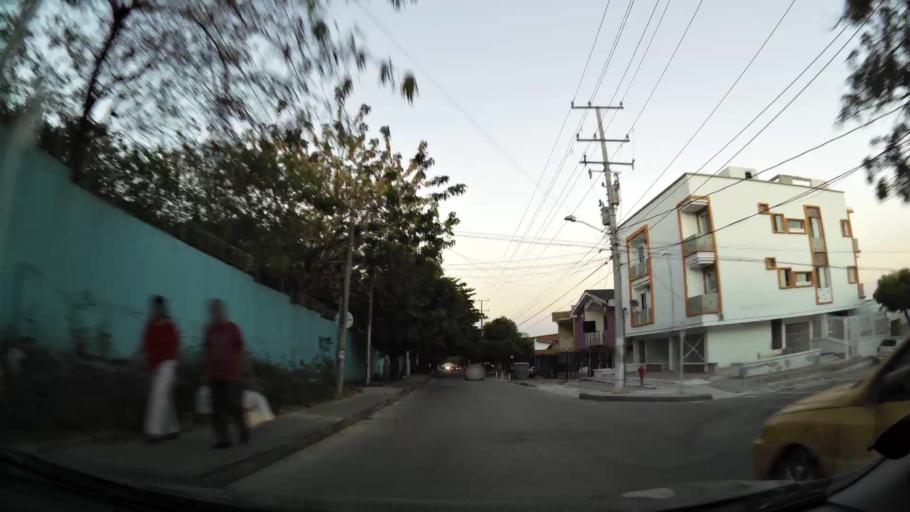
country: CO
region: Atlantico
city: Barranquilla
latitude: 10.9810
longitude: -74.8146
